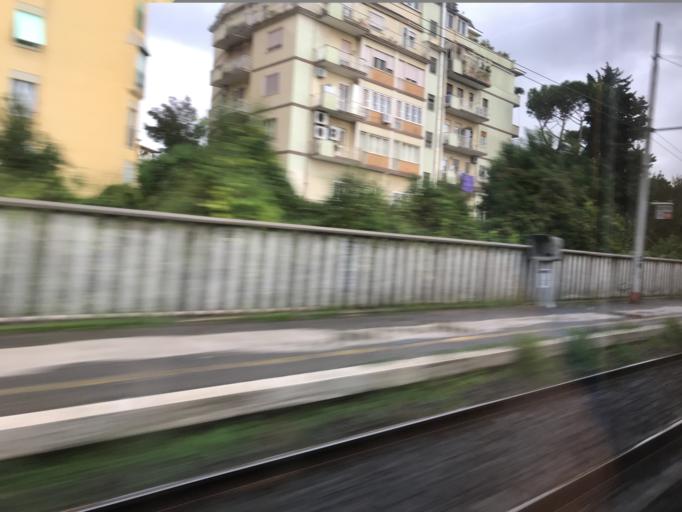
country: IT
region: Latium
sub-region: Citta metropolitana di Roma Capitale
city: Rome
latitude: 41.8722
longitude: 12.4891
